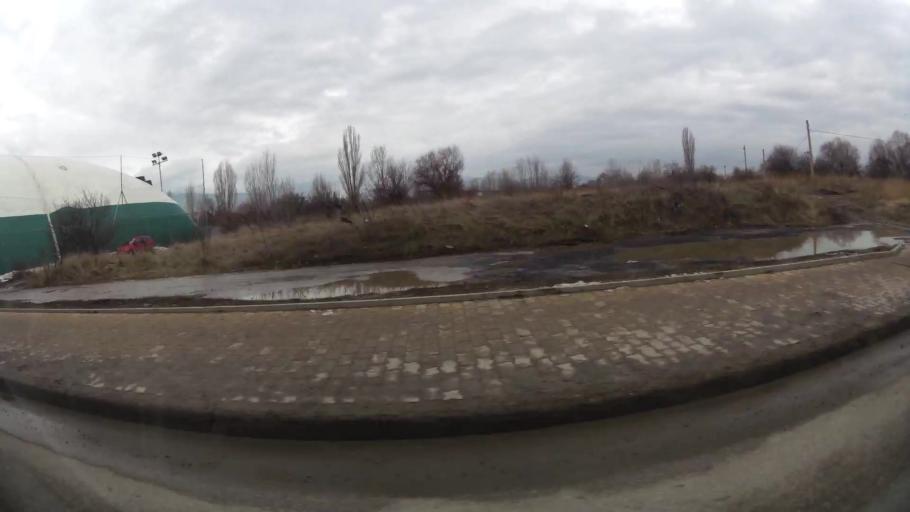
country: BG
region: Sofia-Capital
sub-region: Stolichna Obshtina
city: Sofia
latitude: 42.7412
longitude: 23.2862
